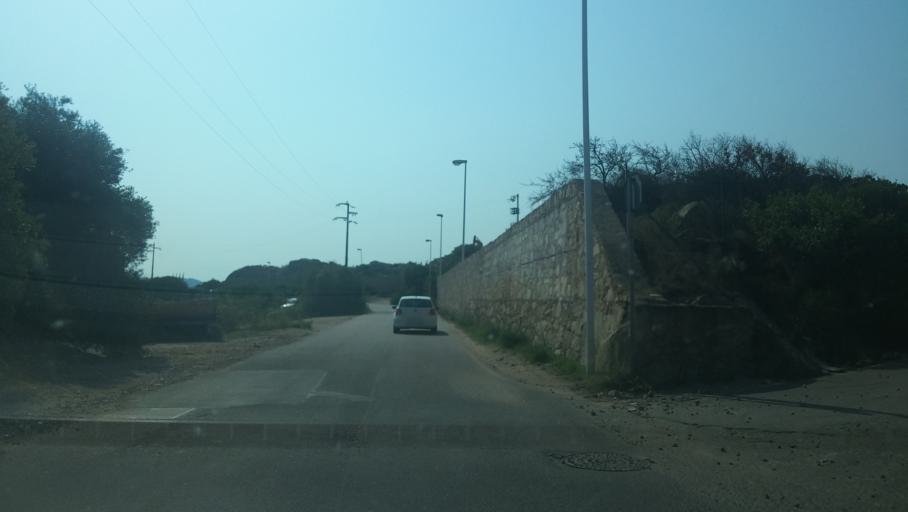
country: IT
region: Sardinia
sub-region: Provincia di Olbia-Tempio
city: La Maddalena
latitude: 41.2188
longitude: 9.4377
